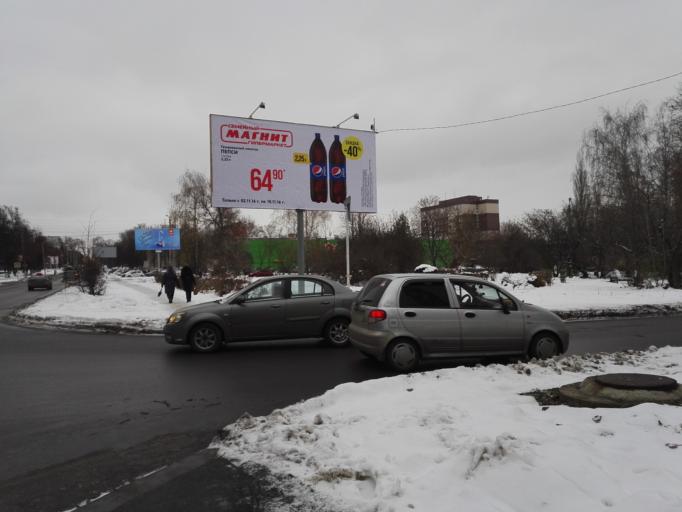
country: RU
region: Tula
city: Novomoskovsk
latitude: 54.0102
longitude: 38.3047
